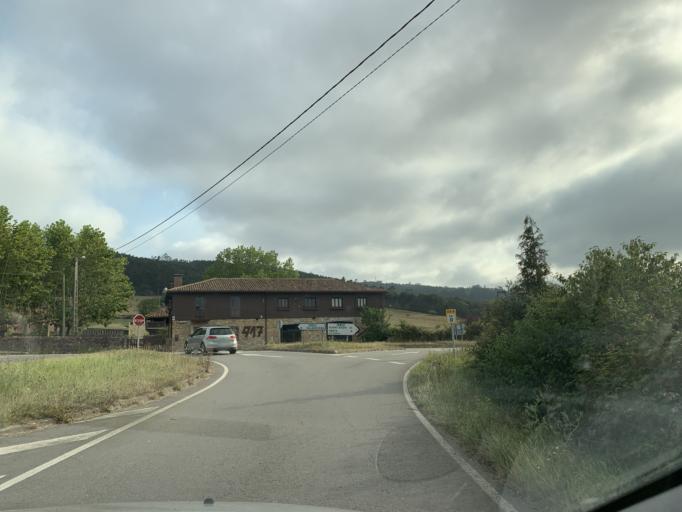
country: ES
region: Asturias
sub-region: Province of Asturias
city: Villaviciosa
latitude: 43.5207
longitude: -5.4394
